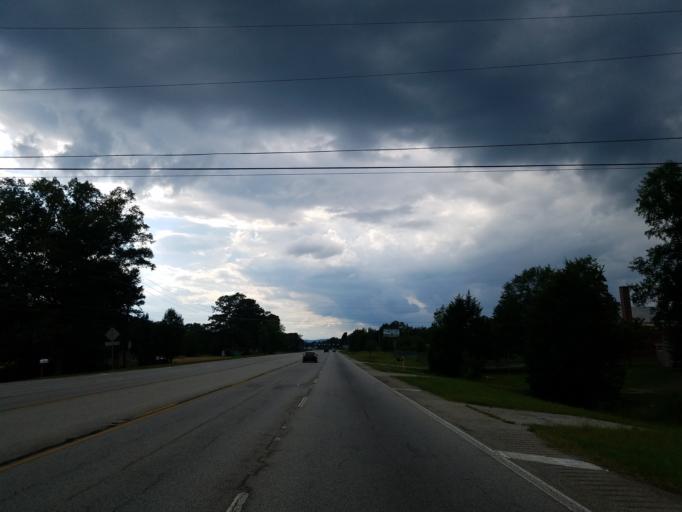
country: US
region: Georgia
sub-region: Floyd County
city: Shannon
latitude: 34.3902
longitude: -85.1846
